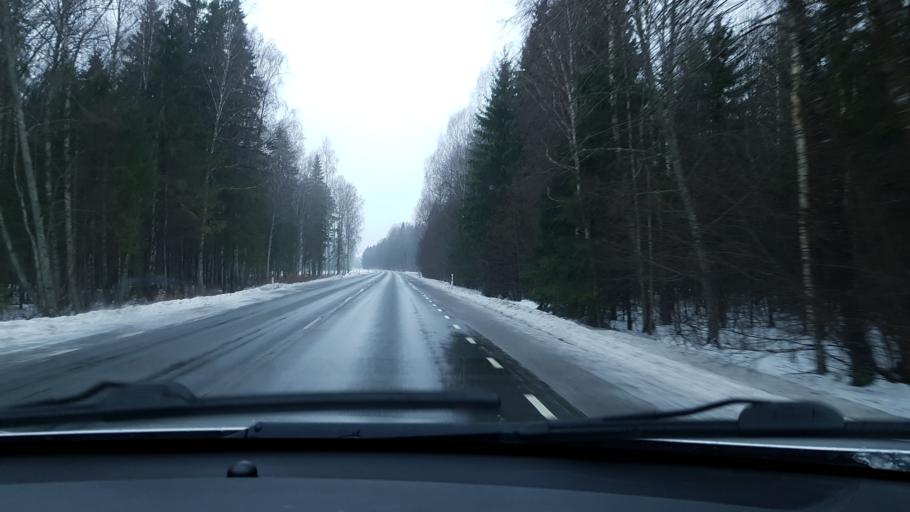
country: EE
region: Jaervamaa
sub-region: Tueri vald
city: Sarevere
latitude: 58.8105
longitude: 25.3406
